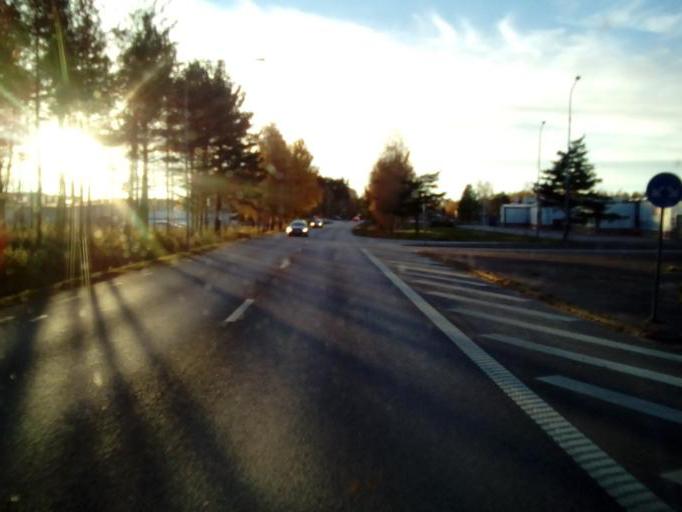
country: SE
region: OErebro
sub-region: Orebro Kommun
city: Orebro
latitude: 59.2146
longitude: 15.1441
